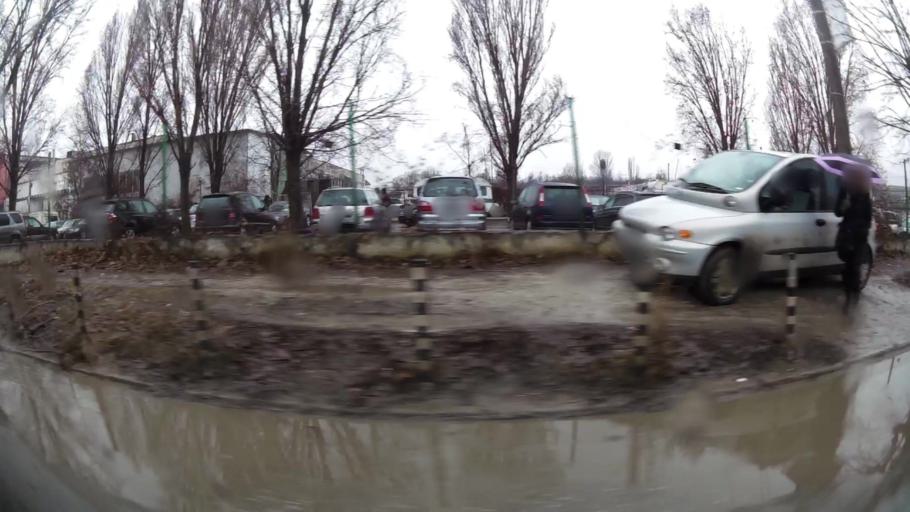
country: BG
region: Sofia-Capital
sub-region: Stolichna Obshtina
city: Sofia
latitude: 42.6409
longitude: 23.4039
